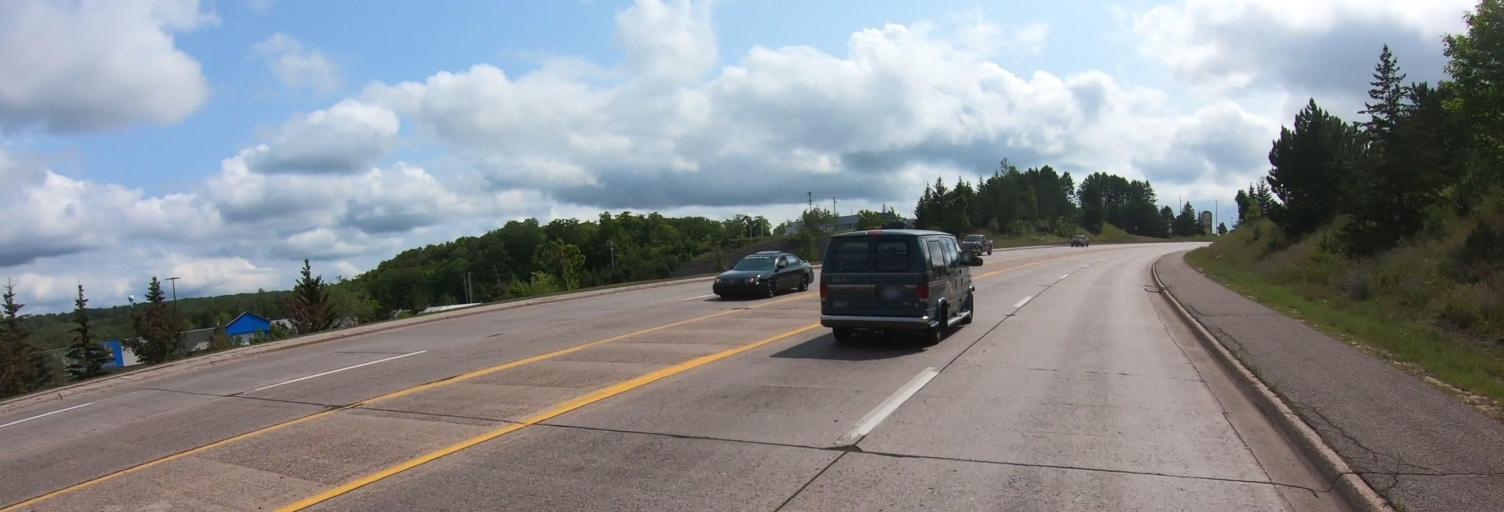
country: US
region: Michigan
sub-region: Houghton County
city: Hancock
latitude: 47.1077
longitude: -88.5908
